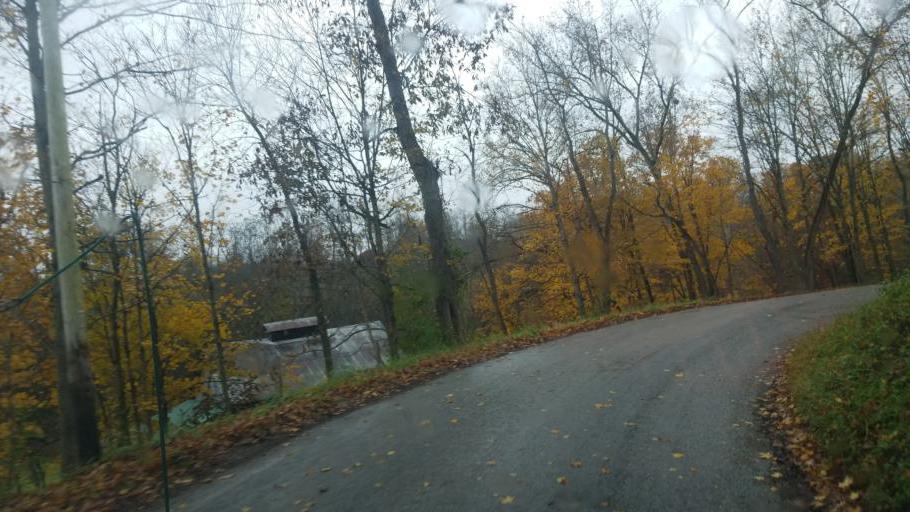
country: US
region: Ohio
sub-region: Washington County
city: Belpre
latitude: 39.3153
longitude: -81.6040
